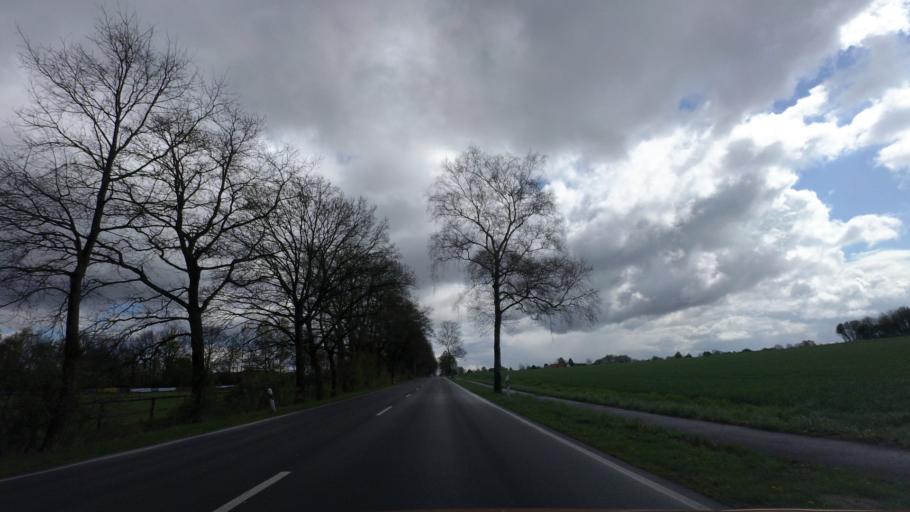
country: DE
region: Lower Saxony
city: Sottrum
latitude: 53.1117
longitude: 9.2187
